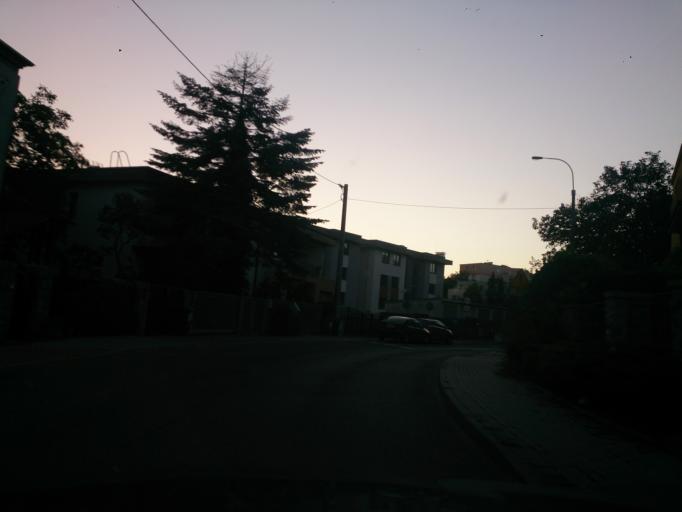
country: PL
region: Pomeranian Voivodeship
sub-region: Gdynia
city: Gdynia
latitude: 54.4910
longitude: 18.5538
